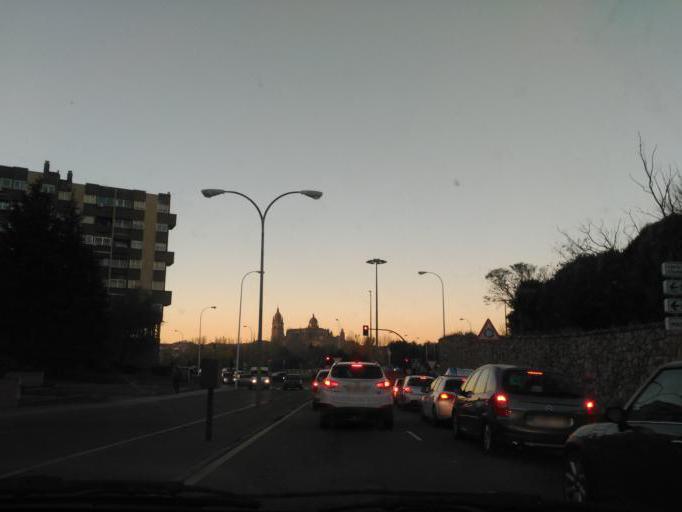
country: ES
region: Castille and Leon
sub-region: Provincia de Salamanca
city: Salamanca
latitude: 40.9517
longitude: -5.6614
